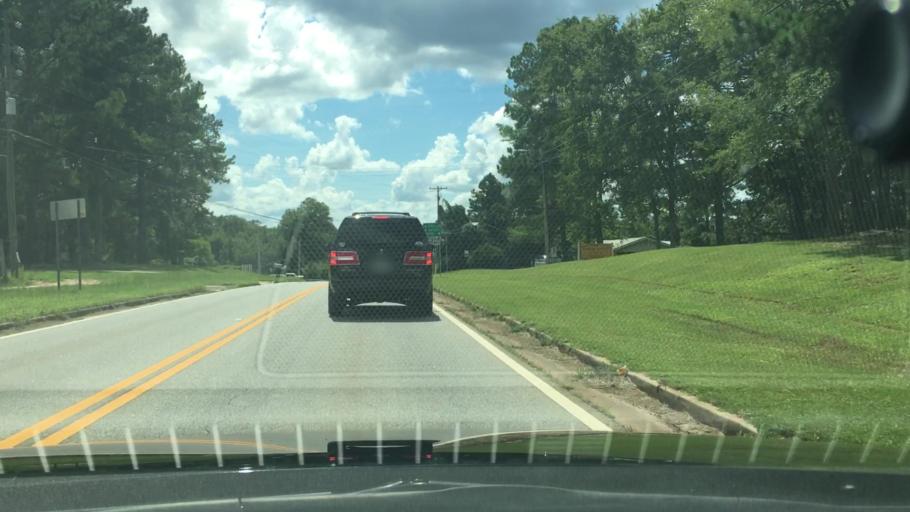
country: US
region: Georgia
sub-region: Putnam County
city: Eatonton
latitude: 33.3202
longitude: -83.4063
